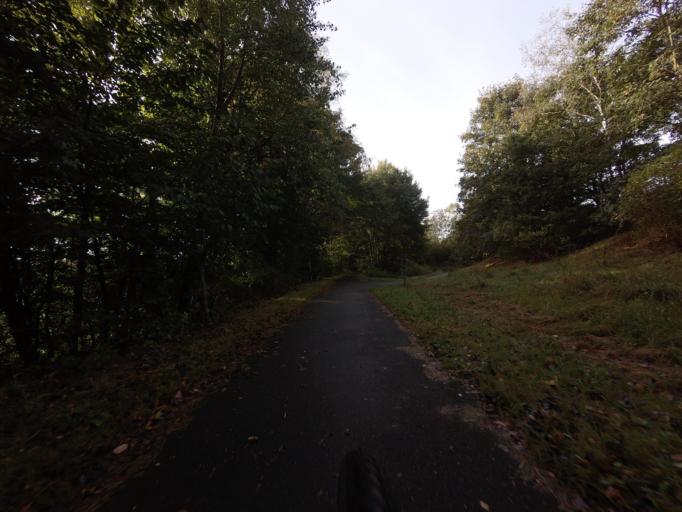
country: DK
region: Central Jutland
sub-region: Viborg Kommune
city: Viborg
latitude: 56.4237
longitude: 9.4525
